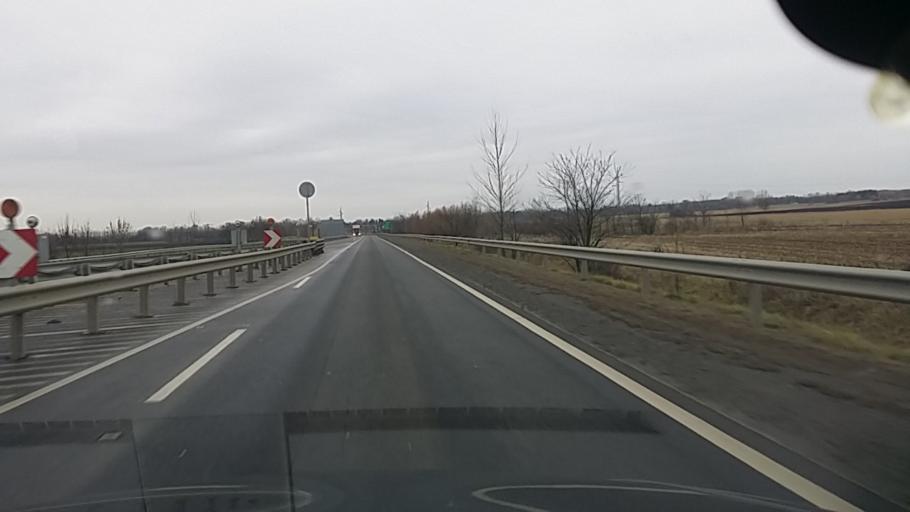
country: HU
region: Szabolcs-Szatmar-Bereg
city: Nyiregyhaza
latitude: 47.8798
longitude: 21.7074
